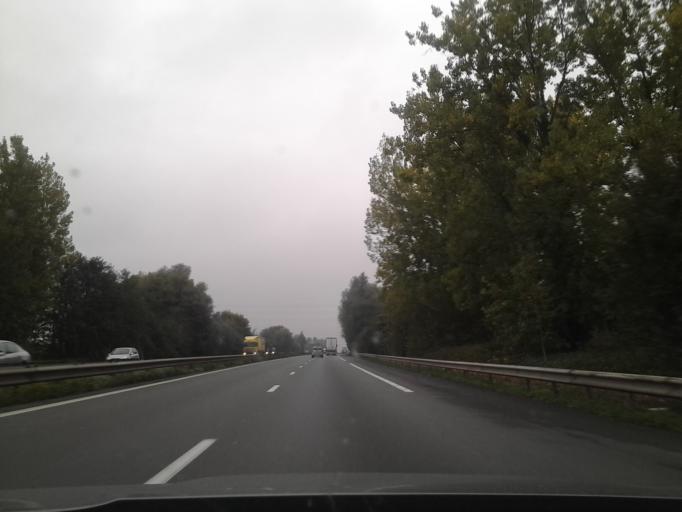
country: FR
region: Nord-Pas-de-Calais
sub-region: Departement du Nord
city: Neuville-sur-Escaut
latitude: 50.2905
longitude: 3.3588
